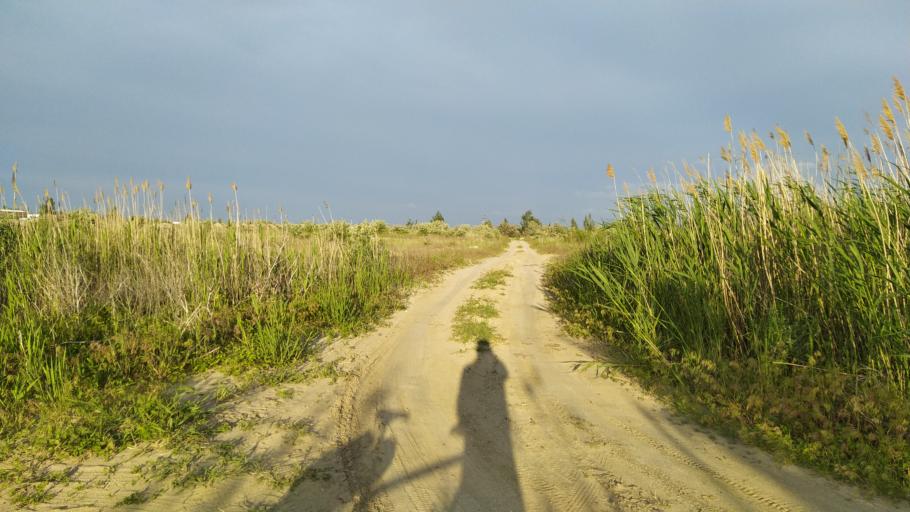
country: RU
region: Rostov
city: Bataysk
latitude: 47.1429
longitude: 39.6676
